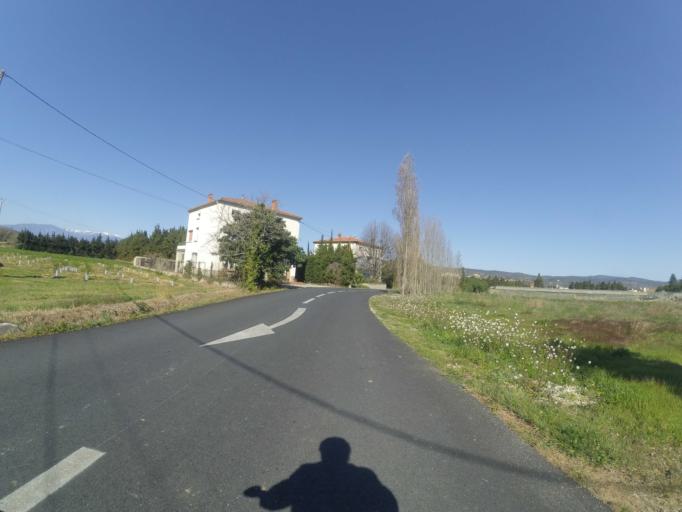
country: FR
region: Languedoc-Roussillon
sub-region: Departement des Pyrenees-Orientales
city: Ille-sur-Tet
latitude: 42.6568
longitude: 2.6215
